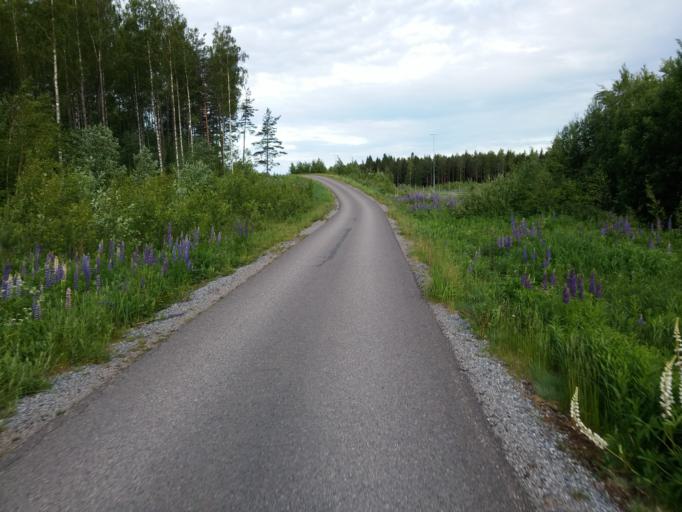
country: FI
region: Uusimaa
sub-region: Helsinki
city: Espoo
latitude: 60.1454
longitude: 24.5698
